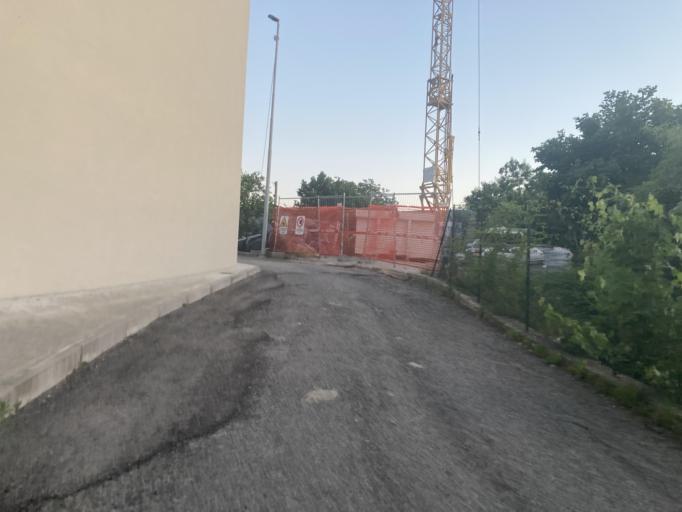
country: IT
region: Abruzzo
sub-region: Provincia dell' Aquila
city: San Demetrio Ne' Vestini
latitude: 42.2920
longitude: 13.5537
